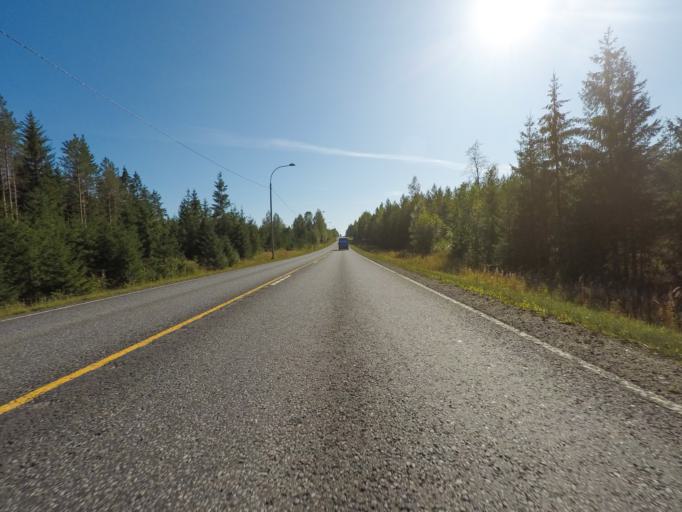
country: FI
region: Southern Savonia
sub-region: Pieksaemaeki
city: Joroinen
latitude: 62.0856
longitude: 27.8233
